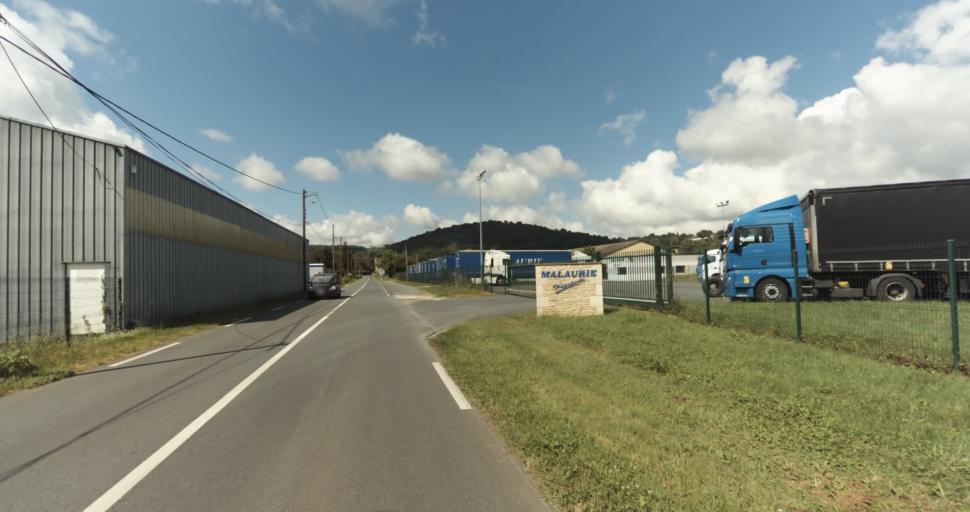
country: FR
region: Aquitaine
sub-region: Departement de la Dordogne
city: Le Bugue
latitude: 44.8499
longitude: 0.9058
